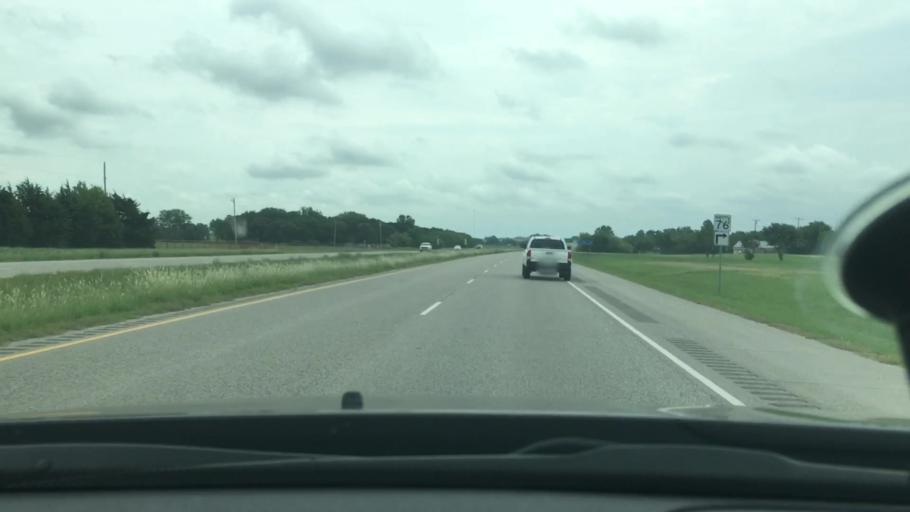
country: US
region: Oklahoma
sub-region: Carter County
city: Wilson
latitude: 34.1733
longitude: -97.4345
